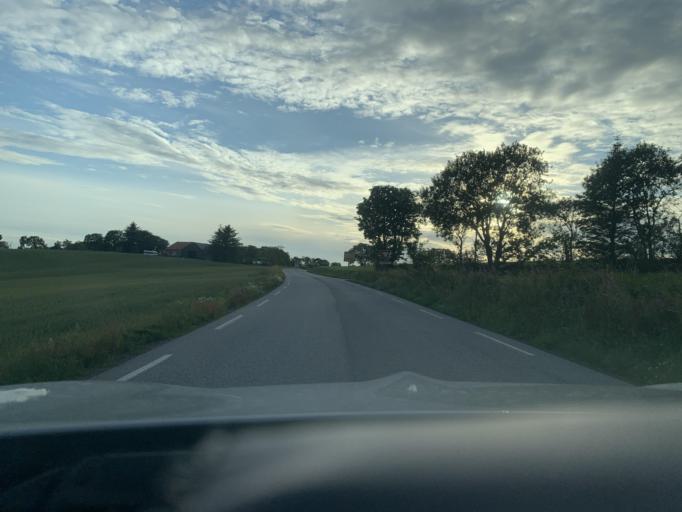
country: NO
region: Rogaland
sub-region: Time
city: Bryne
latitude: 58.6924
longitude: 5.7162
